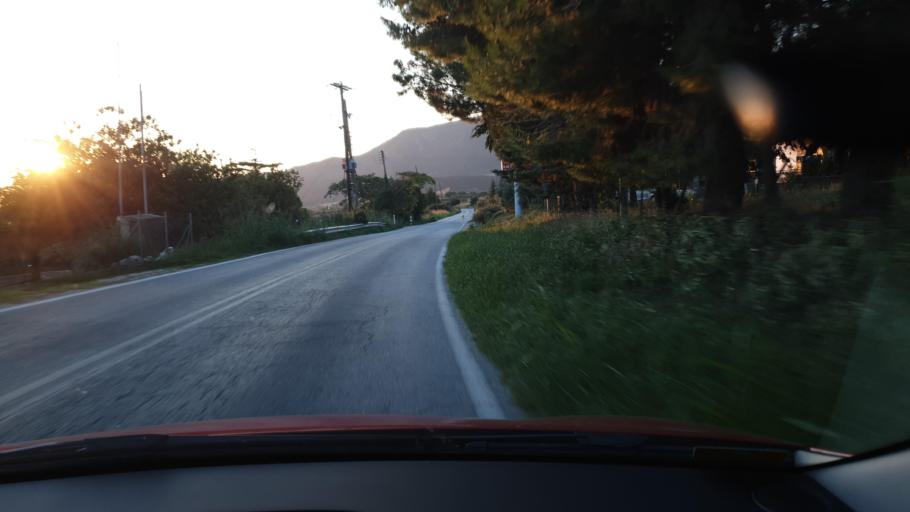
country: GR
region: Central Macedonia
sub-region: Nomos Chalkidikis
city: Galatista
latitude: 40.4681
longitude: 23.2597
